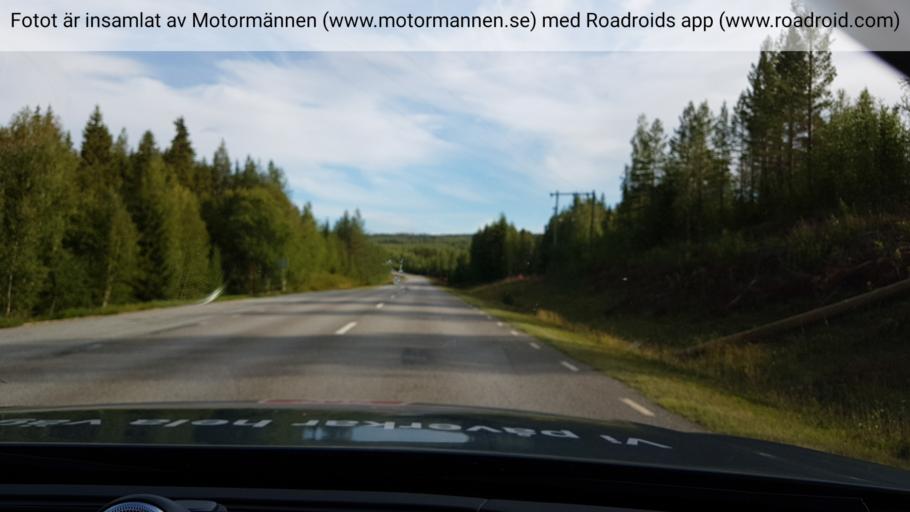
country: SE
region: Jaemtland
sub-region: Stroemsunds Kommun
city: Stroemsund
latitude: 64.2433
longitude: 15.4502
